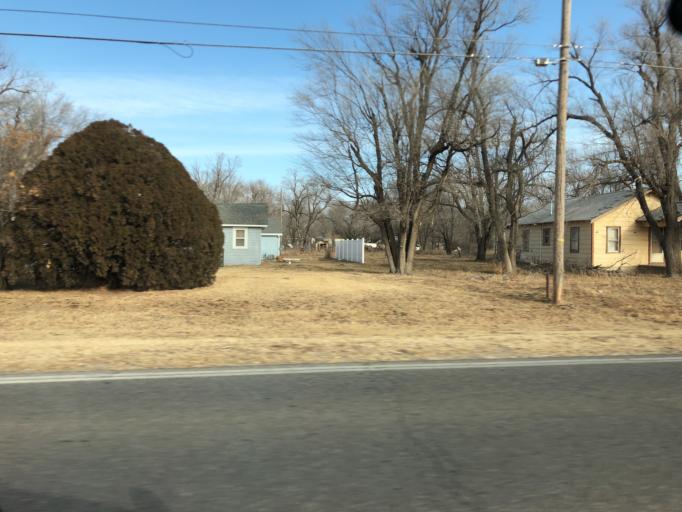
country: US
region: Kansas
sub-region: Reno County
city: South Hutchinson
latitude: 38.0574
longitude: -97.9814
